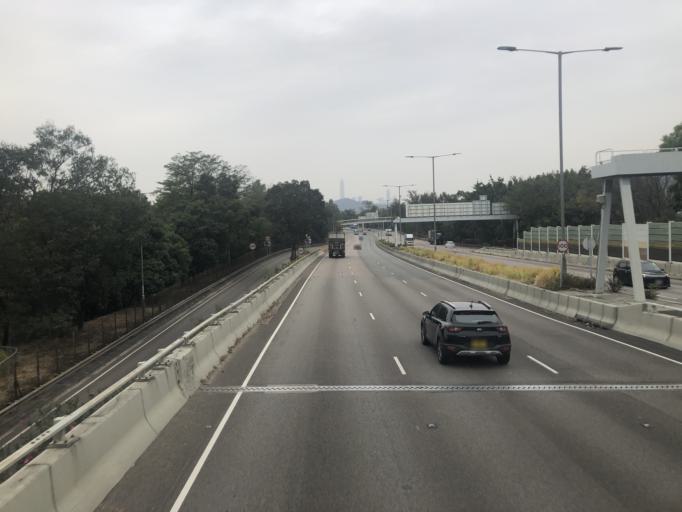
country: HK
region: Tai Po
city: Tai Po
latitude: 22.5005
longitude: 114.1226
